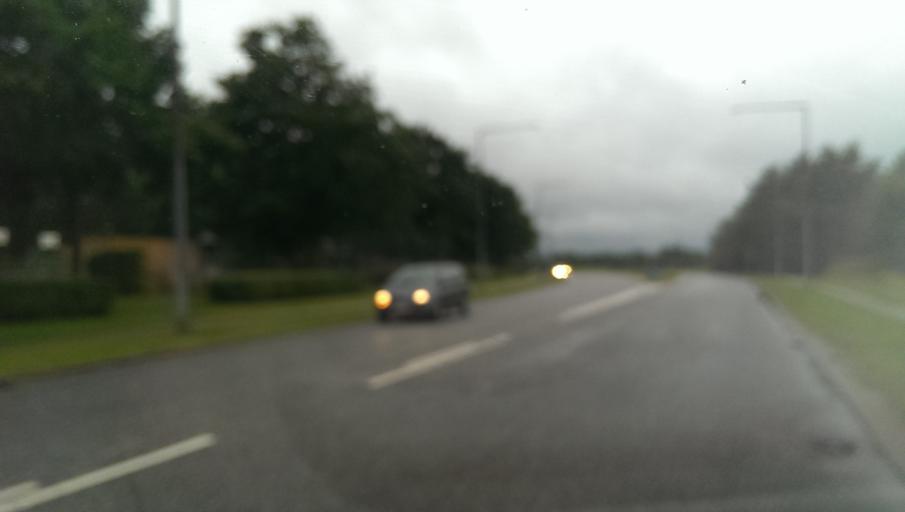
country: DK
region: South Denmark
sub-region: Esbjerg Kommune
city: Esbjerg
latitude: 55.4944
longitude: 8.4884
